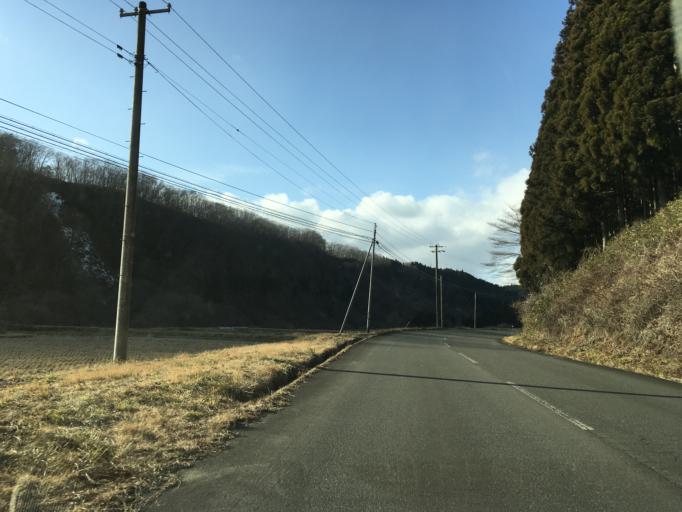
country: JP
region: Miyagi
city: Furukawa
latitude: 38.8001
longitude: 140.8360
